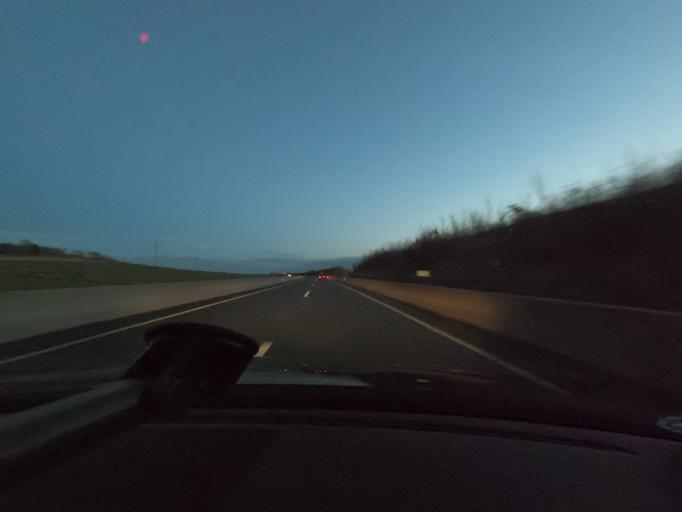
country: DE
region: Lower Saxony
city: Bad Lauterberg im Harz
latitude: 51.5976
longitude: 10.4860
